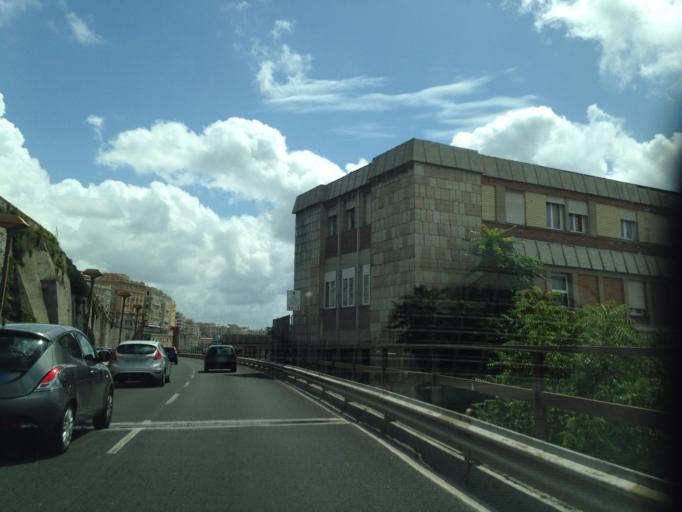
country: IT
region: Liguria
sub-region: Provincia di Genova
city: San Teodoro
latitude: 44.3980
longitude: 8.9357
